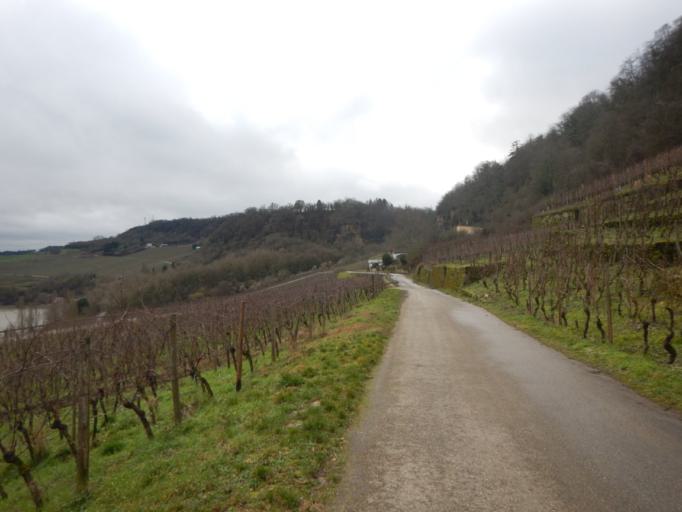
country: DE
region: Rheinland-Pfalz
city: Wellen
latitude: 49.6682
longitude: 6.4255
